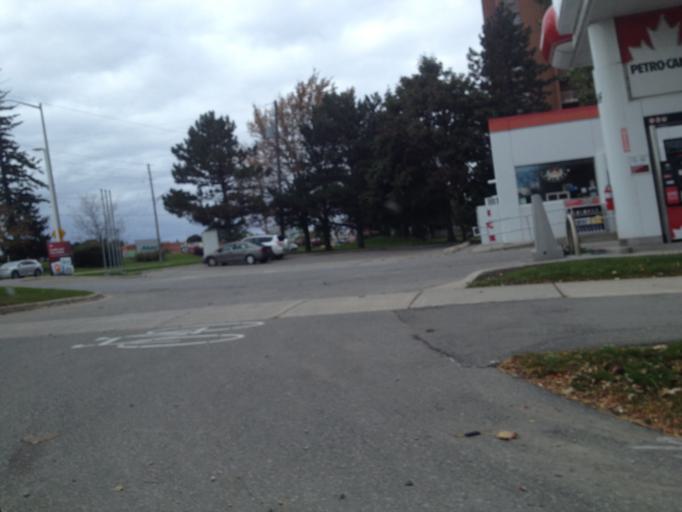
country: CA
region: Ontario
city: London
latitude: 43.0350
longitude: -81.2544
